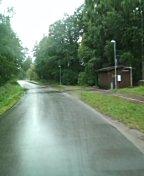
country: SE
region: Vaestmanland
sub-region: Kopings Kommun
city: Koping
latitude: 59.4835
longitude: 16.0563
